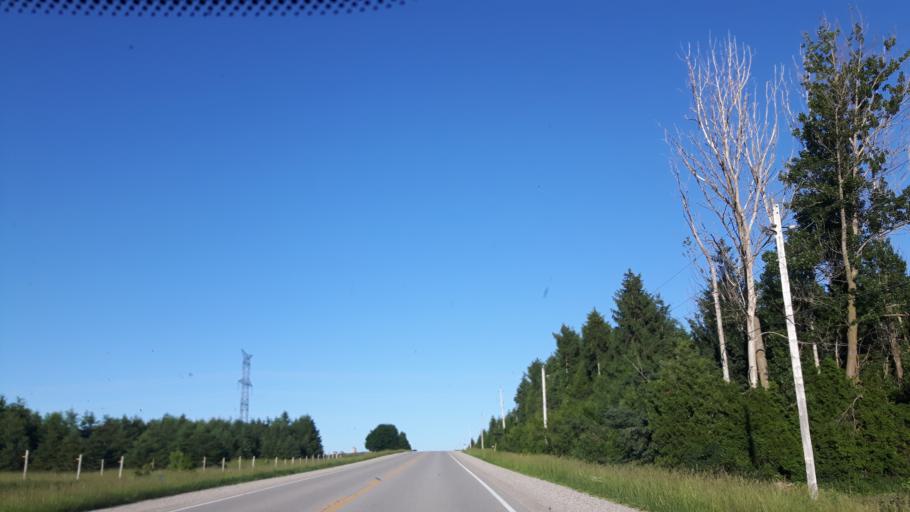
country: CA
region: Ontario
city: Goderich
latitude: 43.6426
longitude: -81.6365
